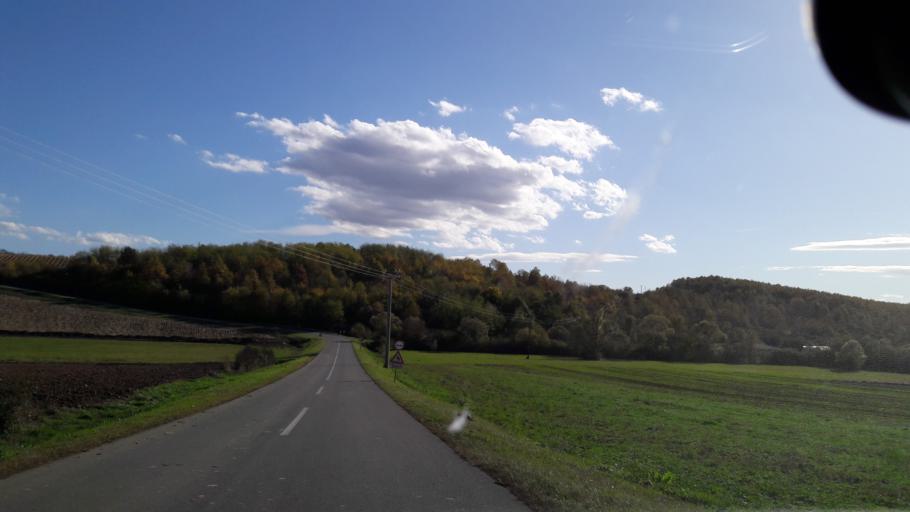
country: HR
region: Osjecko-Baranjska
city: Vukojevci
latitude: 45.3910
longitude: 18.2434
